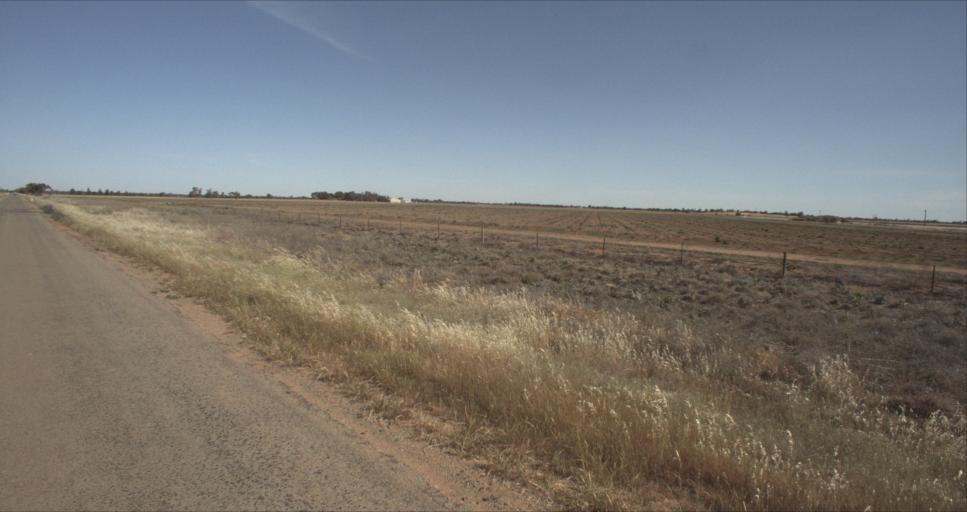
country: AU
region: New South Wales
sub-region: Leeton
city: Leeton
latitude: -34.4796
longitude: 146.3696
